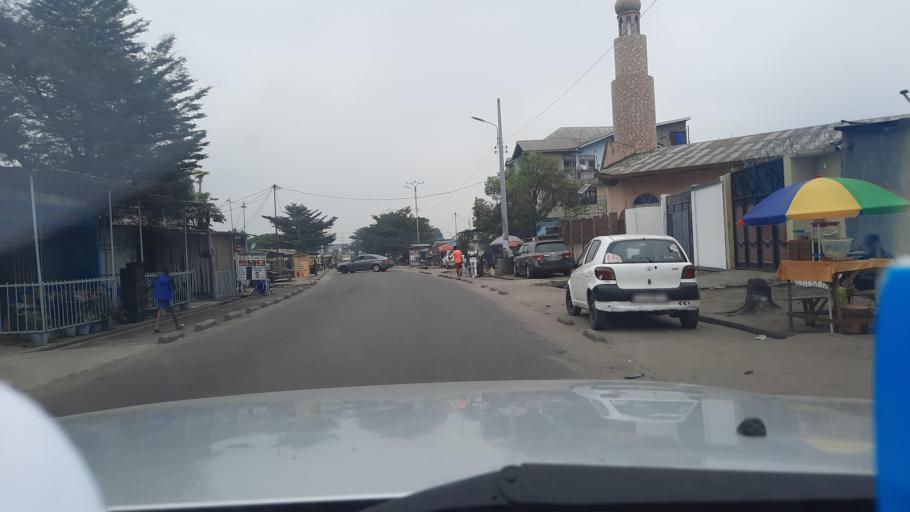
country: CD
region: Kinshasa
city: Masina
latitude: -4.3824
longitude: 15.3449
